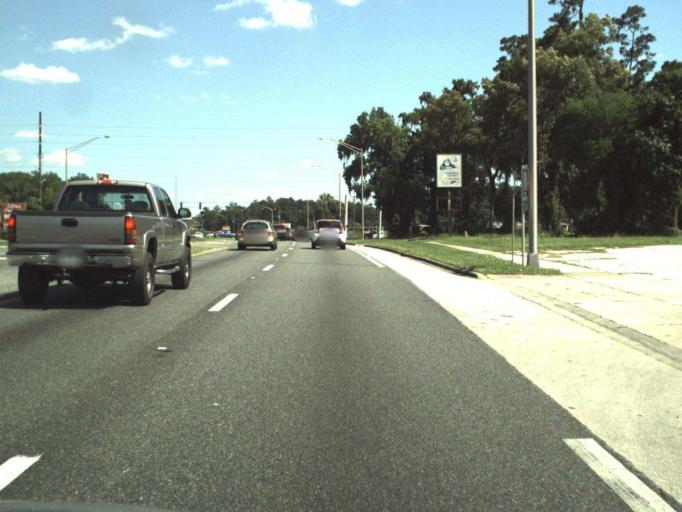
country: US
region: Florida
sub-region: Marion County
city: Ocala
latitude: 29.1583
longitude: -82.1307
